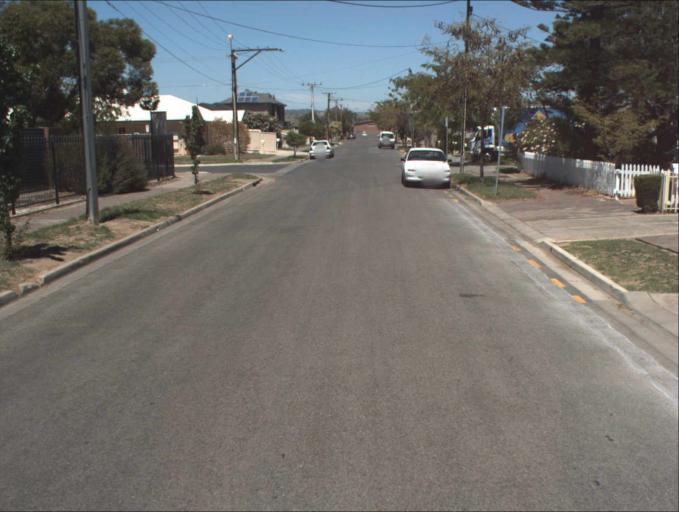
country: AU
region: South Australia
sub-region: Port Adelaide Enfield
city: Klemzig
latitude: -34.8673
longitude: 138.6277
